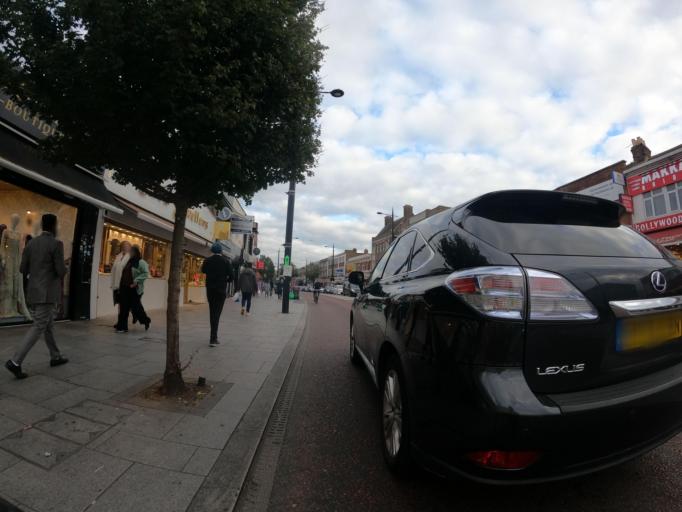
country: GB
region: England
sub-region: Greater London
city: Southall
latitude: 51.5115
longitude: -0.3798
